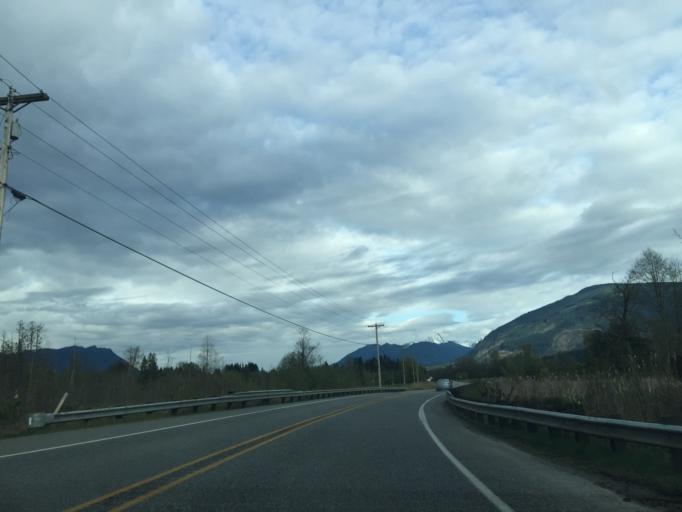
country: US
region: Washington
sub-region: Snohomish County
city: Arlington Heights
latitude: 48.2746
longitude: -121.9954
